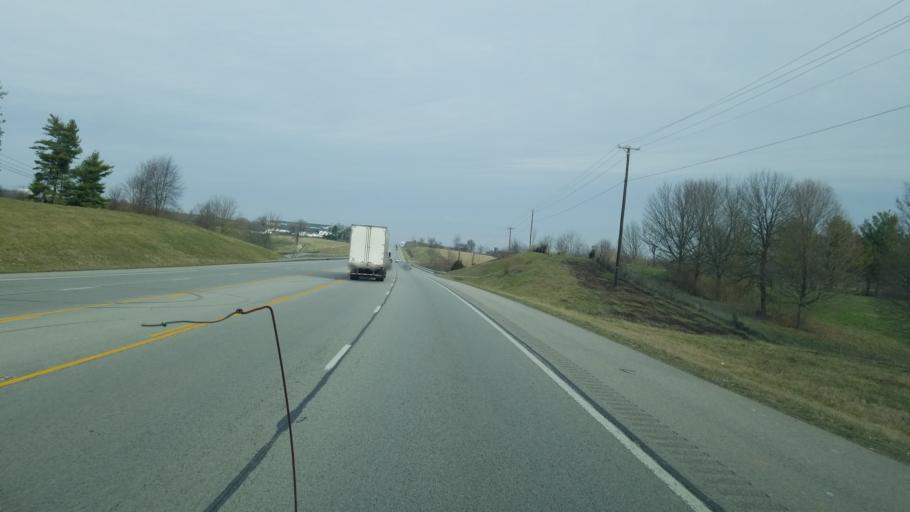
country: US
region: Kentucky
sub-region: Boyle County
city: Junction City
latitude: 37.6019
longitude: -84.7736
